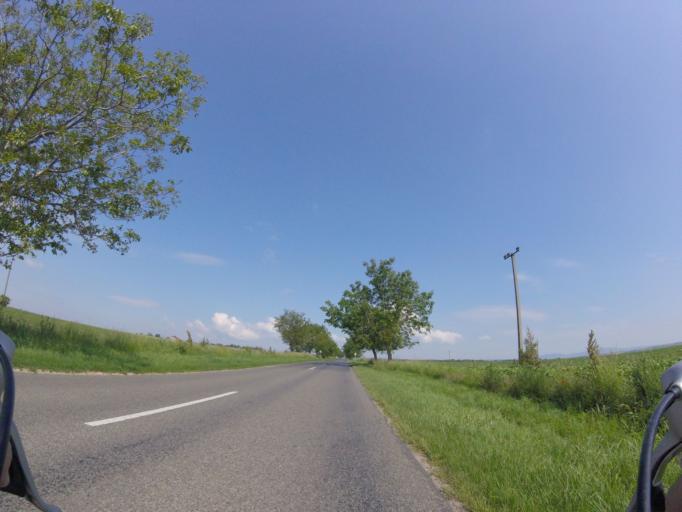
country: HU
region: Baranya
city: Kozarmisleny
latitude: 45.9906
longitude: 18.3270
